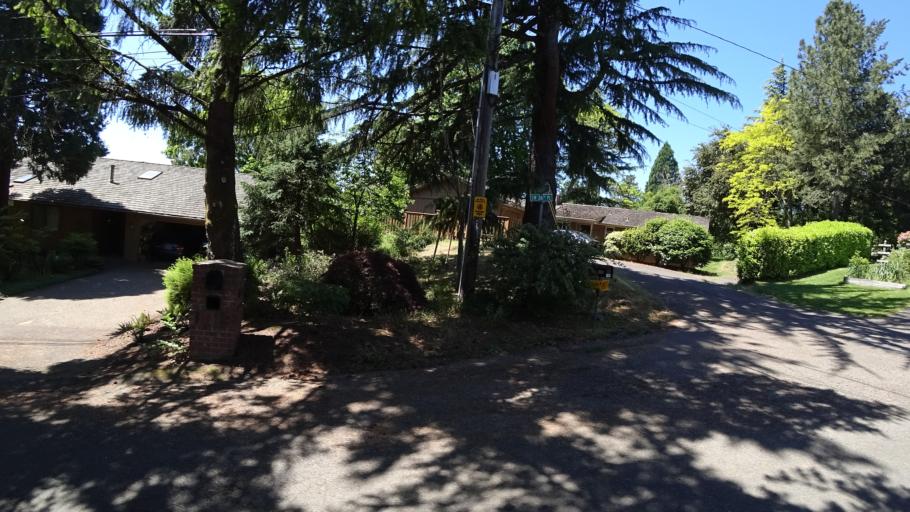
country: US
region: Oregon
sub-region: Washington County
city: Raleigh Hills
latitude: 45.4924
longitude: -122.7145
